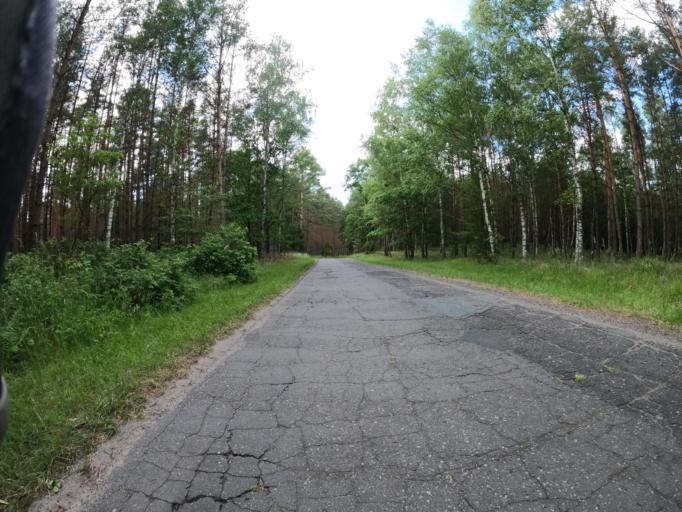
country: PL
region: West Pomeranian Voivodeship
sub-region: Powiat gryfinski
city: Moryn
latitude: 52.7608
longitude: 14.3796
